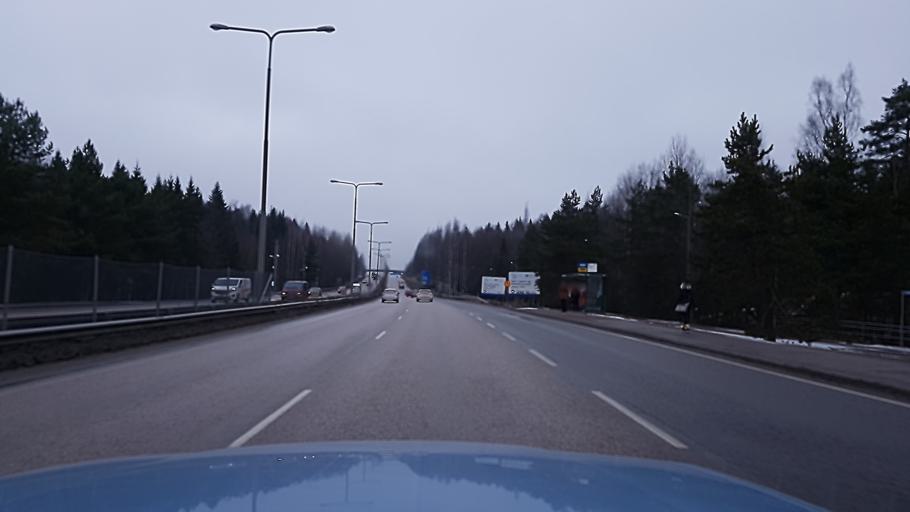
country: FI
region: Uusimaa
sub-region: Helsinki
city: Helsinki
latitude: 60.2281
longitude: 24.9066
